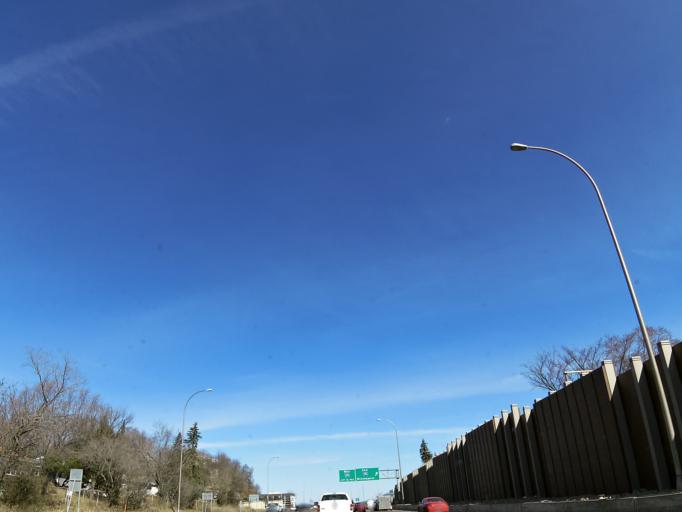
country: US
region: Minnesota
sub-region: Hennepin County
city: Minnetonka Mills
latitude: 44.9684
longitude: -93.4006
